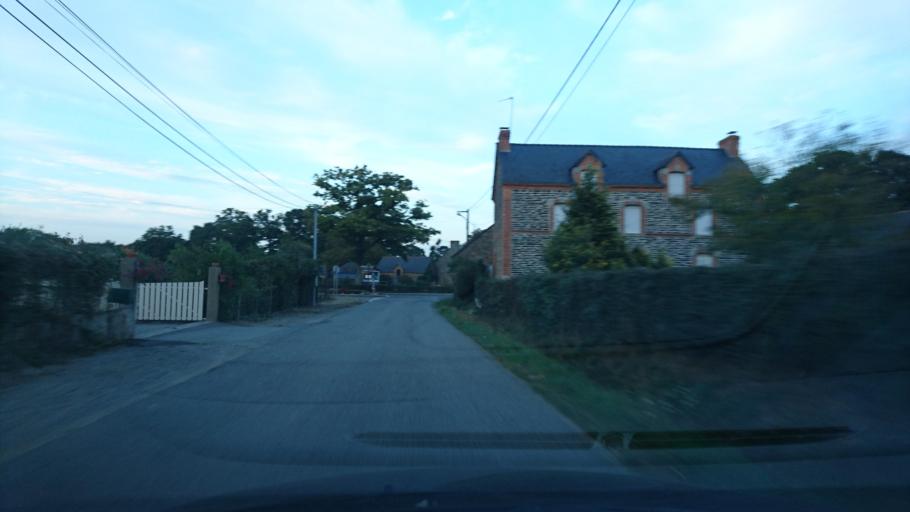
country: FR
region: Brittany
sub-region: Departement d'Ille-et-Vilaine
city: Pipriac
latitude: 47.8499
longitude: -1.9456
